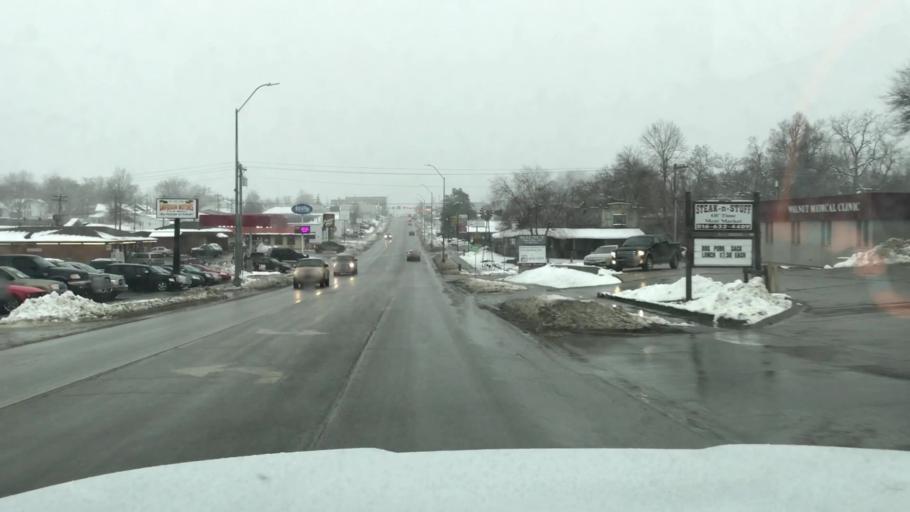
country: US
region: Missouri
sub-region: Clinton County
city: Cameron
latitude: 39.7461
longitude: -94.2356
